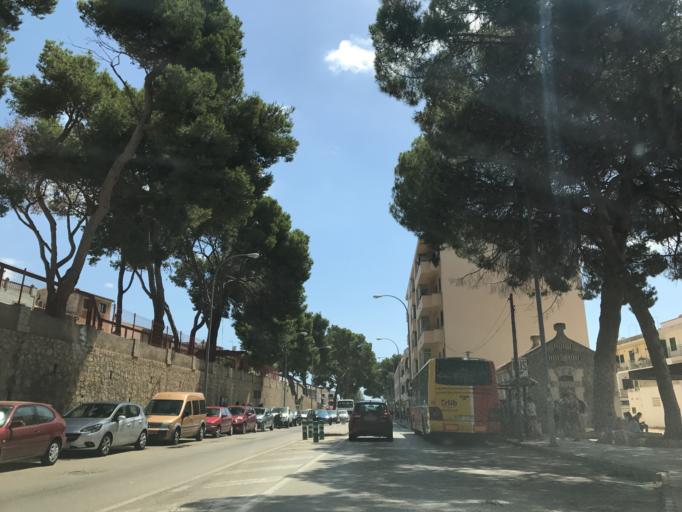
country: ES
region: Balearic Islands
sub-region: Illes Balears
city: Arta
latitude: 39.6910
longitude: 3.3498
